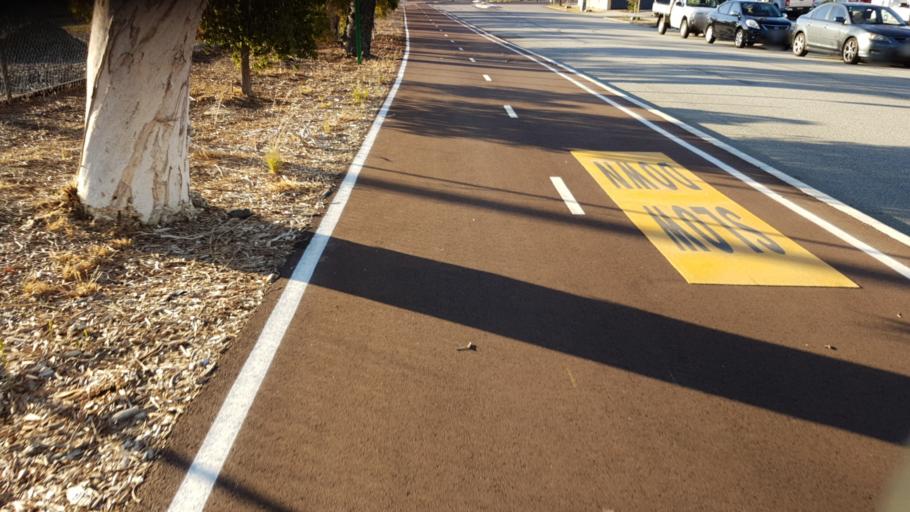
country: AU
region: Western Australia
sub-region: Victoria Park
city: Victoria Park
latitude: -31.9801
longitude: 115.9117
